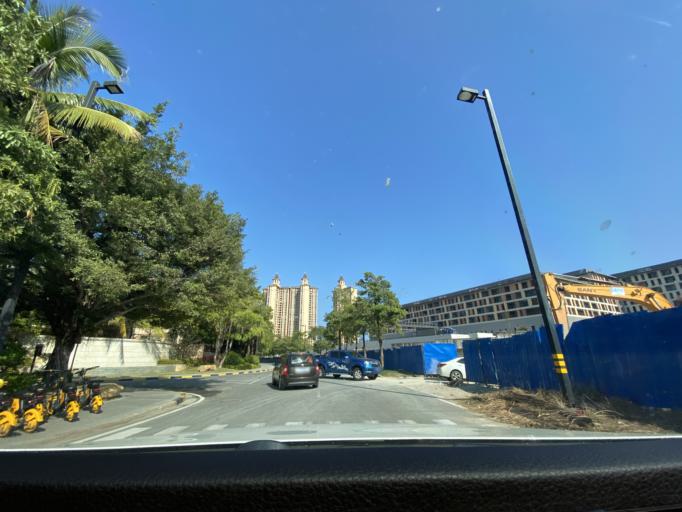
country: CN
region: Hainan
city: Yingzhou
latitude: 18.4113
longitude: 109.8835
